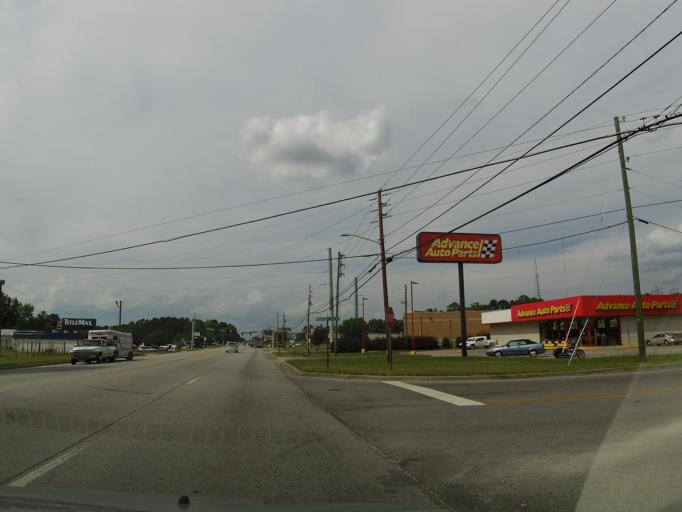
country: US
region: Georgia
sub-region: McDuffie County
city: Thomson
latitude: 33.4825
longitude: -82.5053
